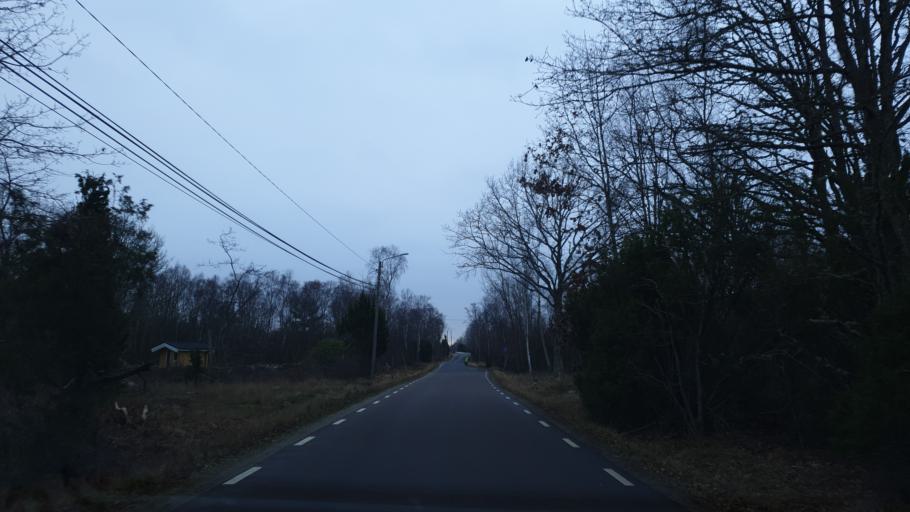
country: SE
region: Blekinge
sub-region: Karlskrona Kommun
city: Karlskrona
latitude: 56.1152
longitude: 15.6144
